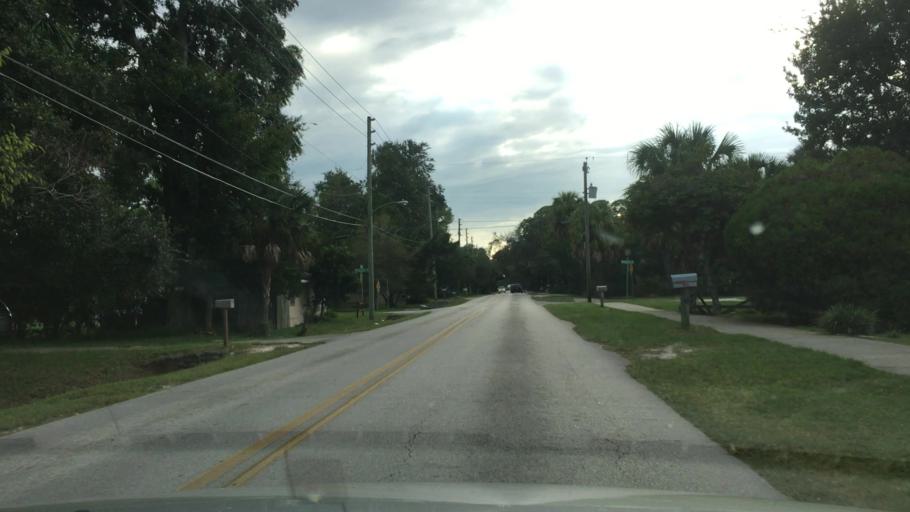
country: US
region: Florida
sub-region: Volusia County
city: Holly Hill
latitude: 29.2516
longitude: -81.0567
